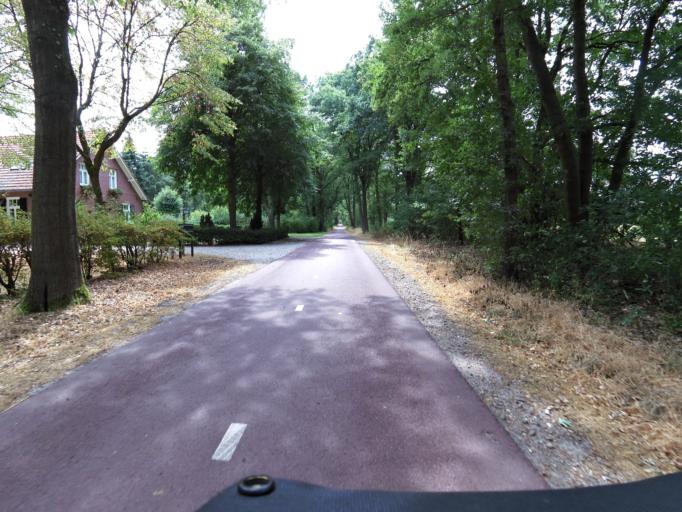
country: NL
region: Limburg
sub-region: Gemeente Venlo
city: Arcen
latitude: 51.5177
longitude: 6.1832
